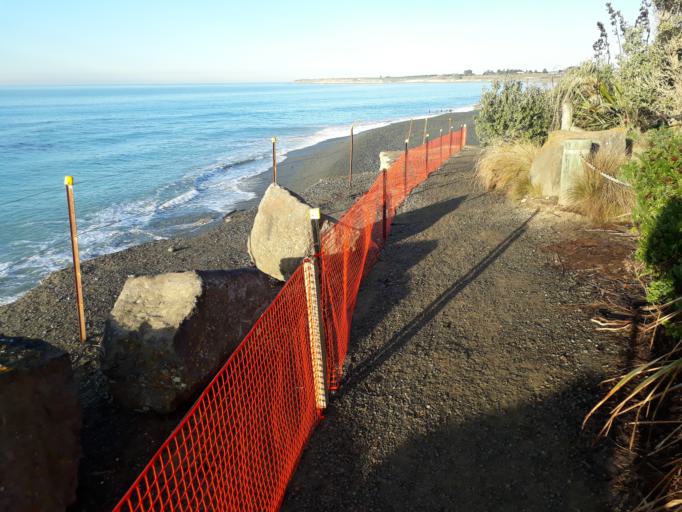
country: NZ
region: Canterbury
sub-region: Timaru District
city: Timaru
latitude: -44.4155
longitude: 171.2639
